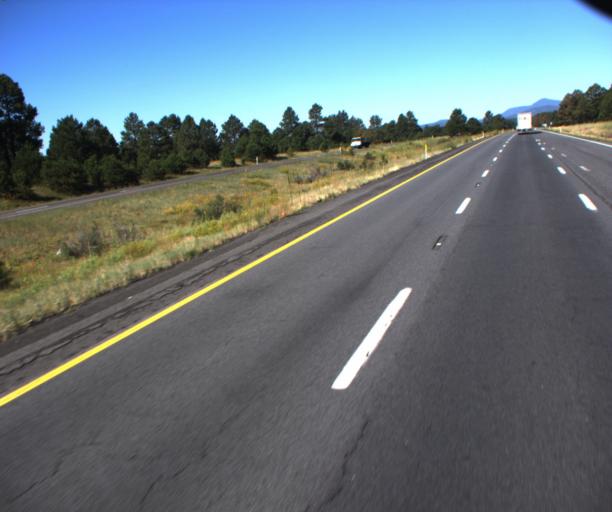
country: US
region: Arizona
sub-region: Coconino County
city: Parks
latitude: 35.2543
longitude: -111.9449
